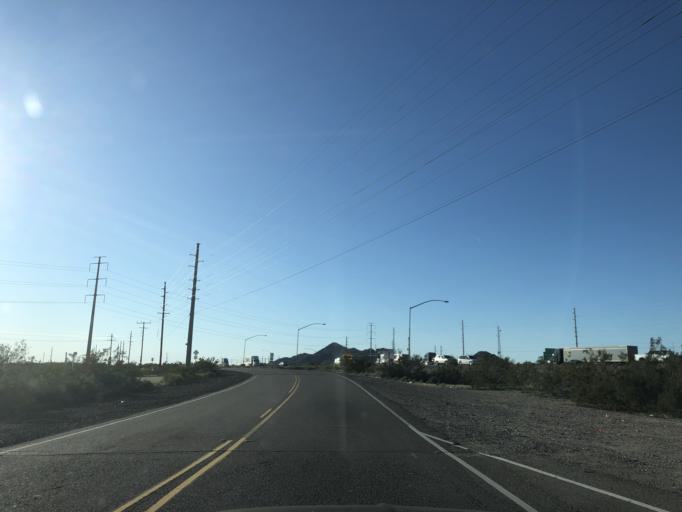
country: US
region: Arizona
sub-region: Maricopa County
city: Buckeye
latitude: 33.4354
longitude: -112.5830
